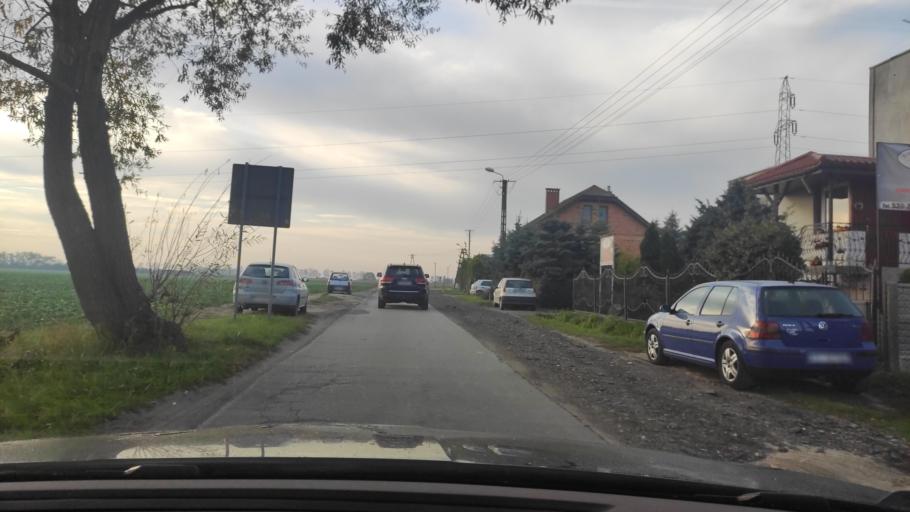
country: PL
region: Greater Poland Voivodeship
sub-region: Powiat poznanski
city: Kleszczewo
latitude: 52.3777
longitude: 17.1664
